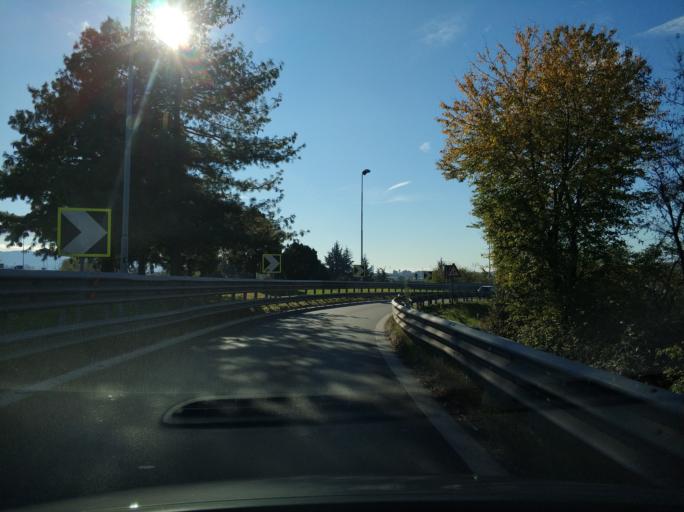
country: IT
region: Piedmont
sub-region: Provincia di Torino
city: Borgaro Torinese
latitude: 45.1278
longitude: 7.6951
